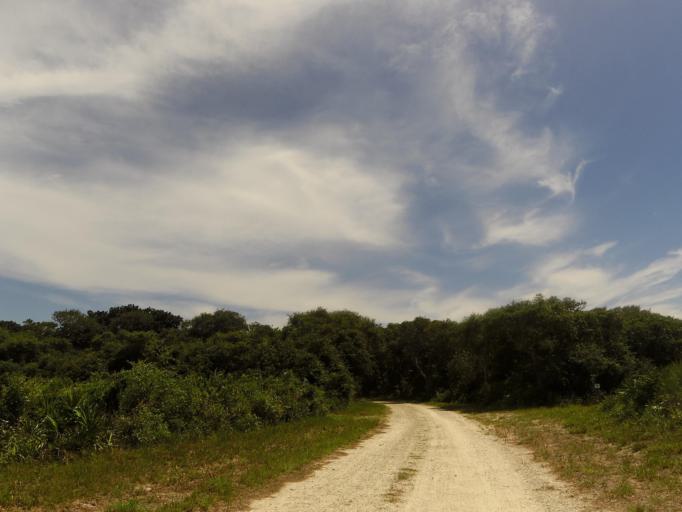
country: US
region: Florida
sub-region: Saint Johns County
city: Villano Beach
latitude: 30.0361
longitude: -81.3359
